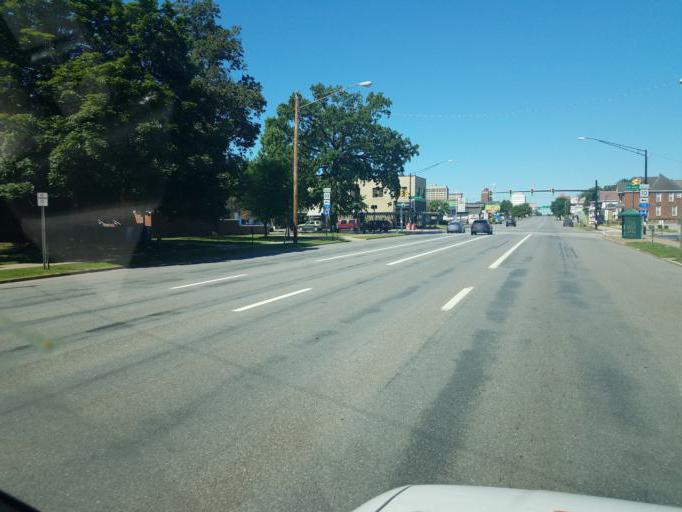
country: US
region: West Virginia
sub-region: Cabell County
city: Huntington
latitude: 38.4242
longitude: -82.4313
